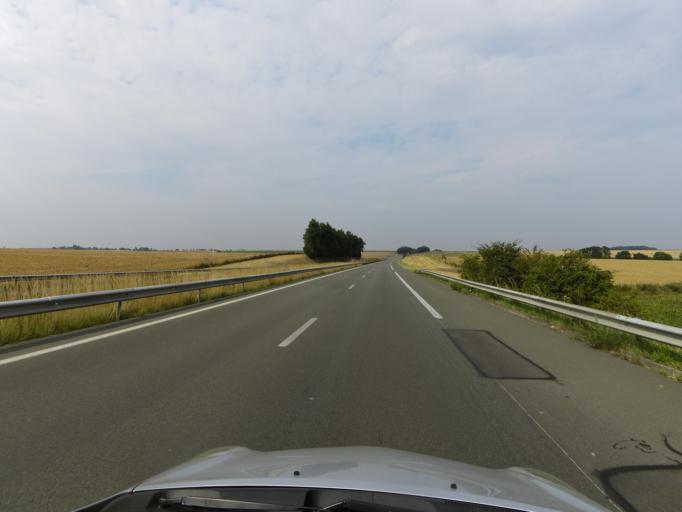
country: FR
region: Picardie
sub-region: Departement de la Somme
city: Epehy
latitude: 50.0226
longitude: 3.1706
